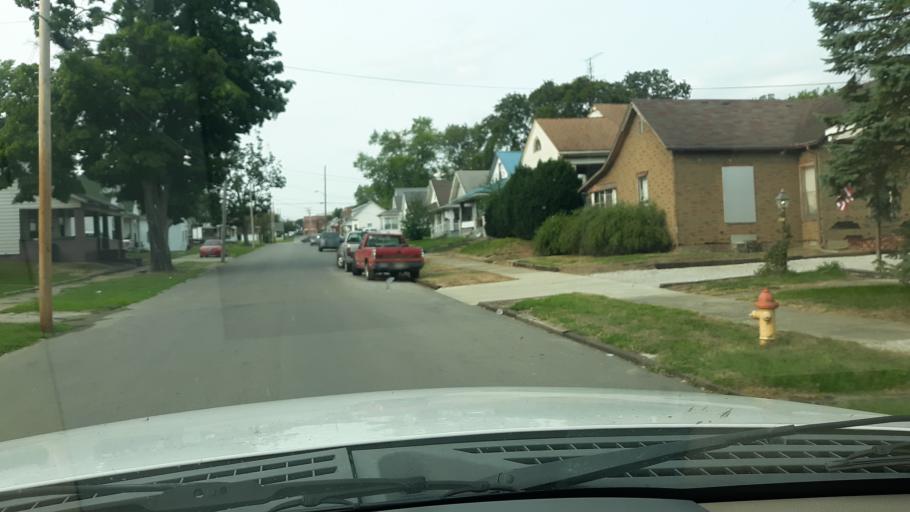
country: US
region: Indiana
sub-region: Gibson County
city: Princeton
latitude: 38.3529
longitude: -87.5638
